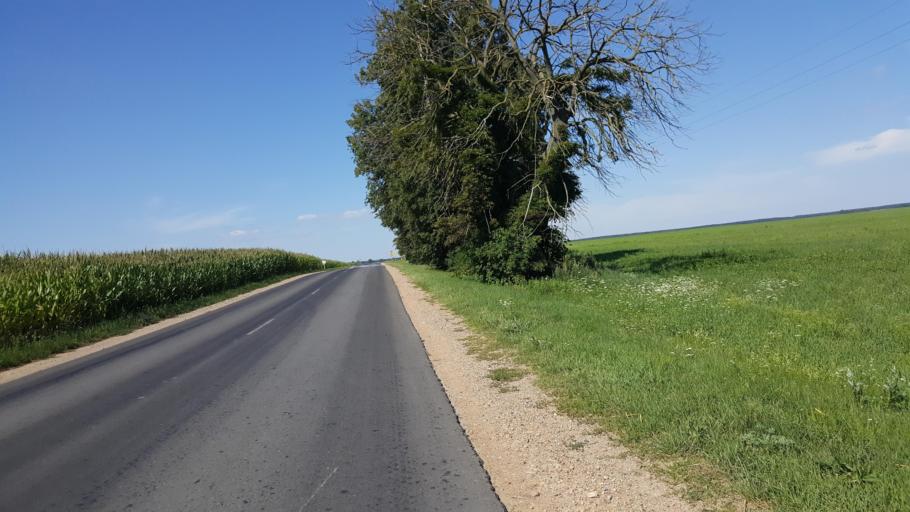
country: BY
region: Brest
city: Charnawchytsy
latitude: 52.2857
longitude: 23.6041
